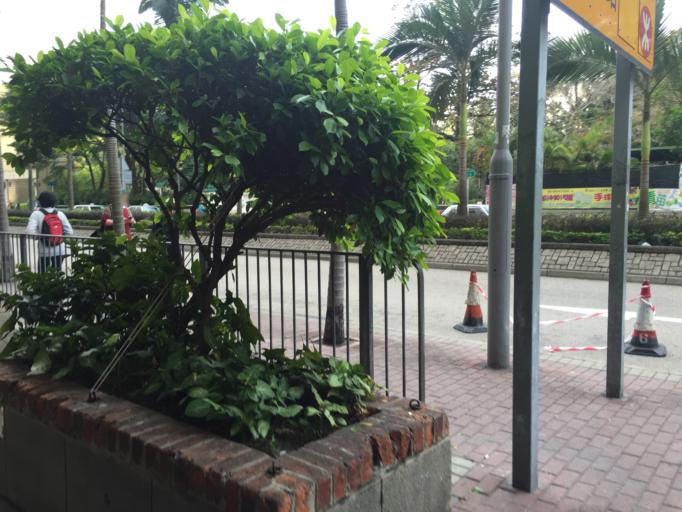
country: HK
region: Sham Shui Po
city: Sham Shui Po
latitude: 22.3390
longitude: 114.1384
